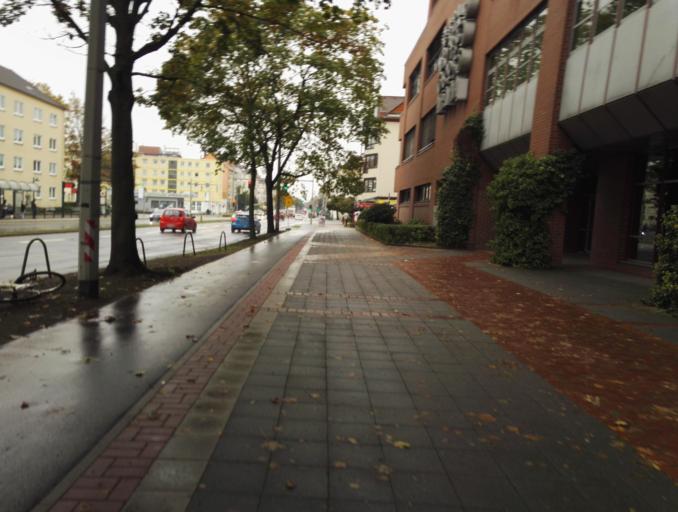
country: DE
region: Lower Saxony
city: Braunschweig
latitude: 52.2737
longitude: 10.5364
